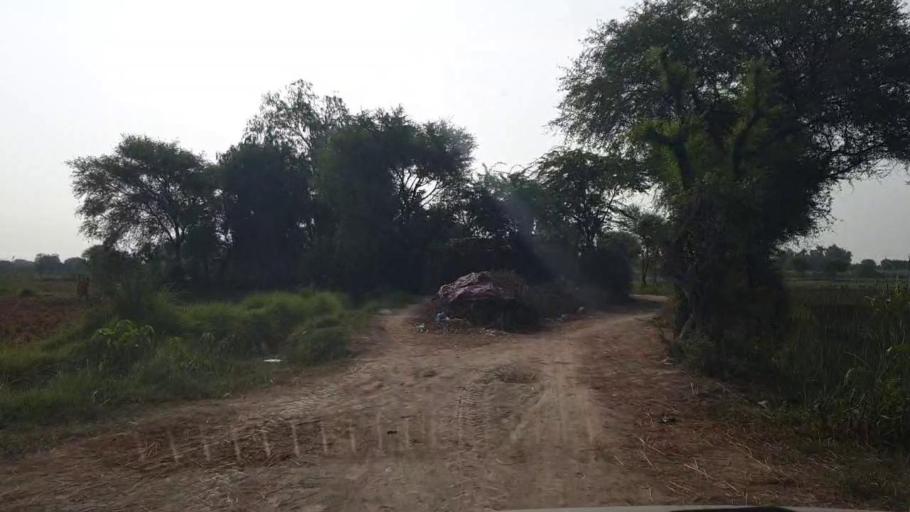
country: PK
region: Sindh
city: Rajo Khanani
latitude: 24.9078
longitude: 68.9203
